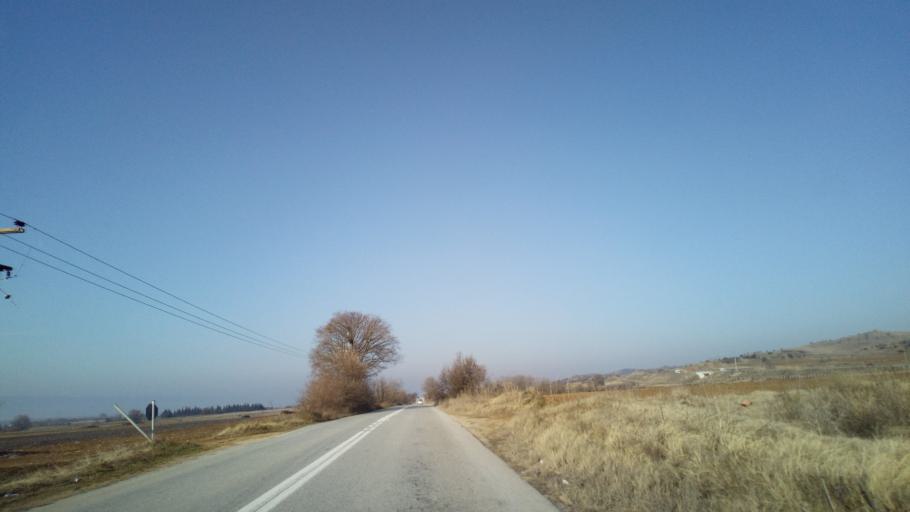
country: GR
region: Central Macedonia
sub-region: Nomos Thessalonikis
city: Gerakarou
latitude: 40.6860
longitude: 23.2391
